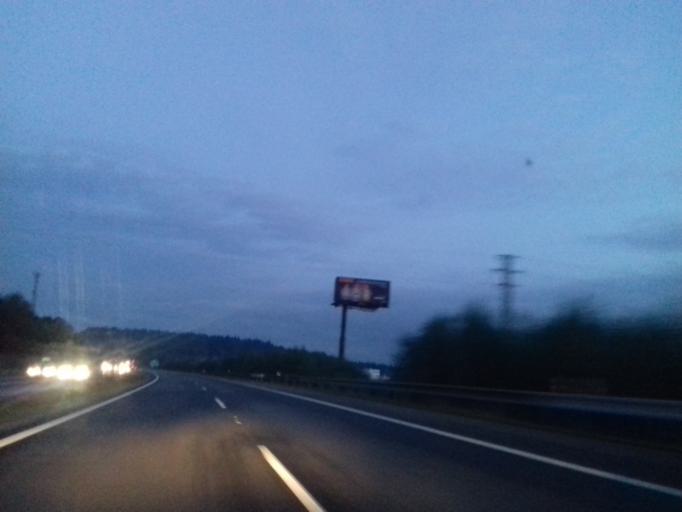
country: CZ
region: Vysocina
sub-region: Okres Pelhrimov
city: Humpolec
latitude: 49.5283
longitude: 15.3429
